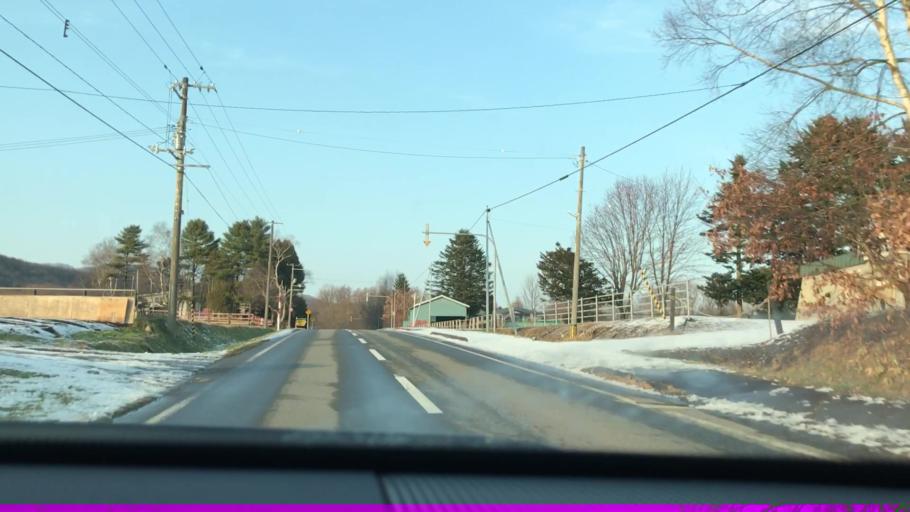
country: JP
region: Hokkaido
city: Shizunai-furukawacho
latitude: 42.4270
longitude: 142.4038
